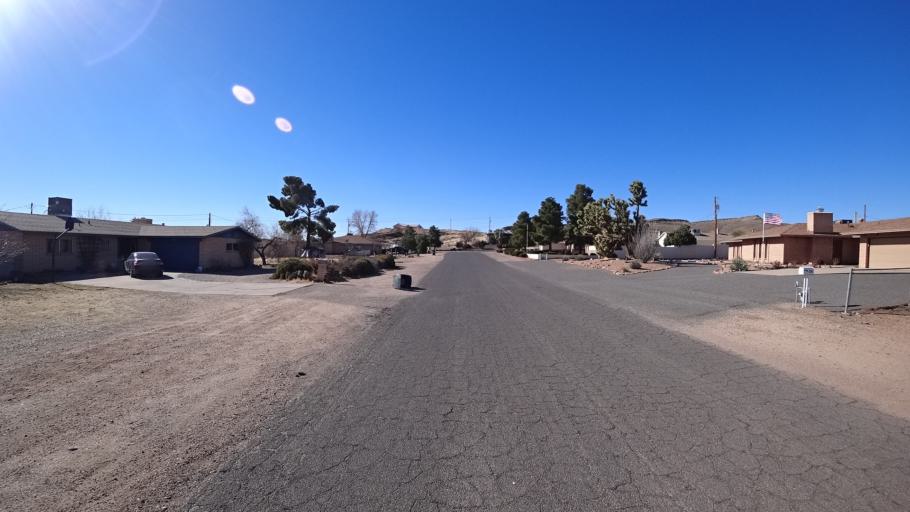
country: US
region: Arizona
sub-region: Mohave County
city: New Kingman-Butler
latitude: 35.2307
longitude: -114.0444
